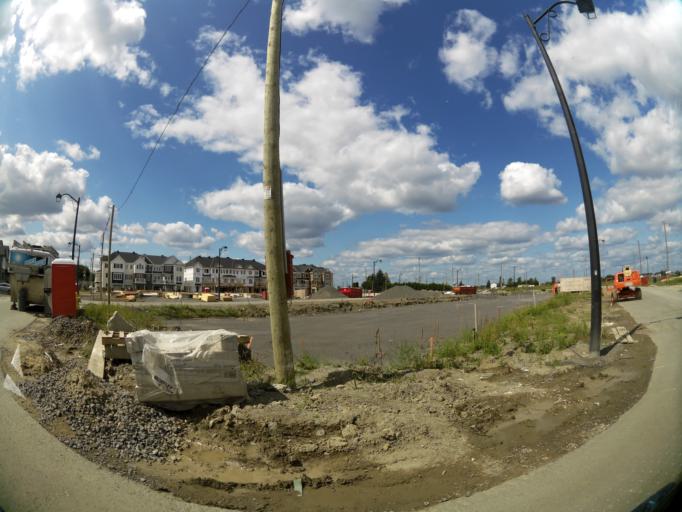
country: CA
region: Ontario
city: Ottawa
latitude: 45.4392
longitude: -75.4928
